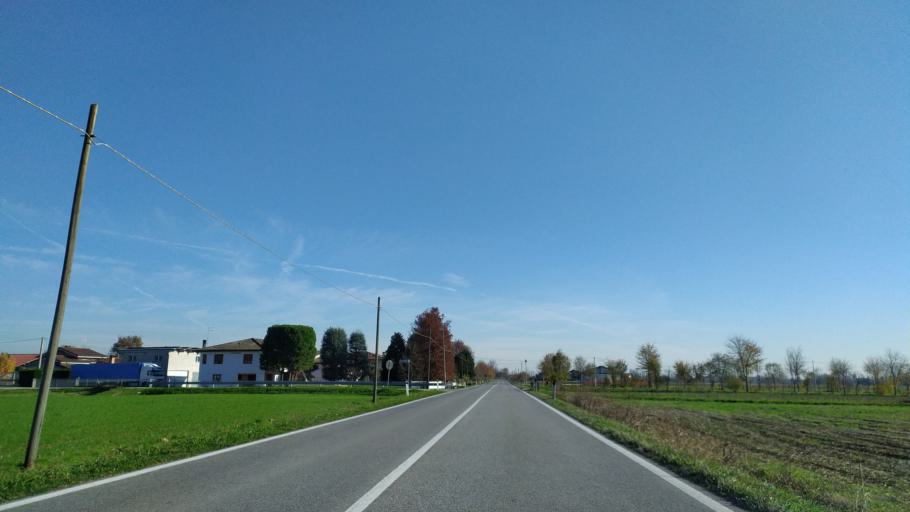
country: IT
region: Veneto
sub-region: Provincia di Padova
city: San Giorgio in Bosco
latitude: 45.5876
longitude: 11.8268
